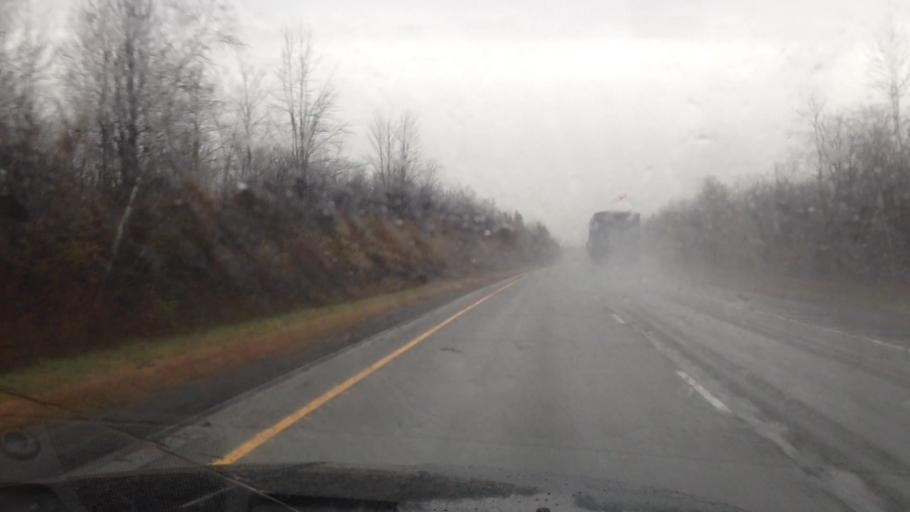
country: CA
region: Ontario
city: Casselman
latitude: 45.3147
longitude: -75.1931
